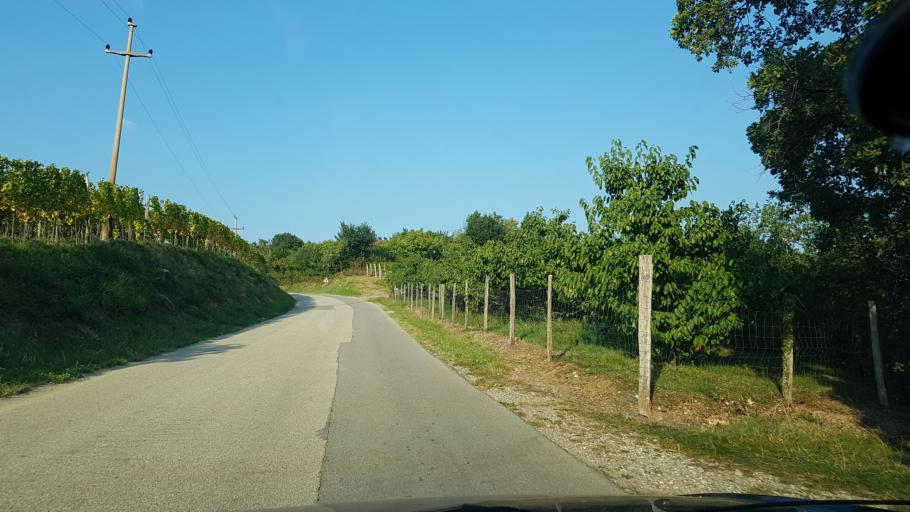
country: IT
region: Friuli Venezia Giulia
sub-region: Provincia di Gorizia
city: San Floriano del Collio
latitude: 45.9838
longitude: 13.5721
